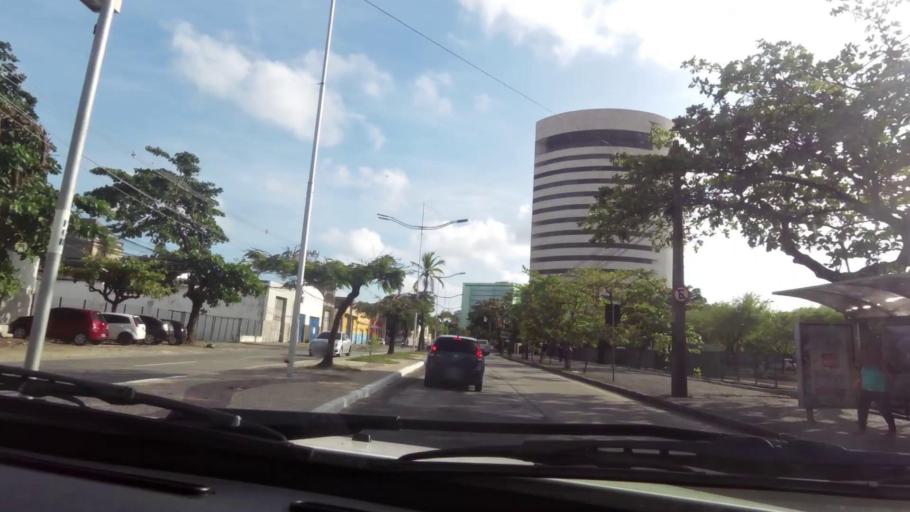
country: BR
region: Pernambuco
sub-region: Recife
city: Recife
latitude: -8.0592
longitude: -34.8727
